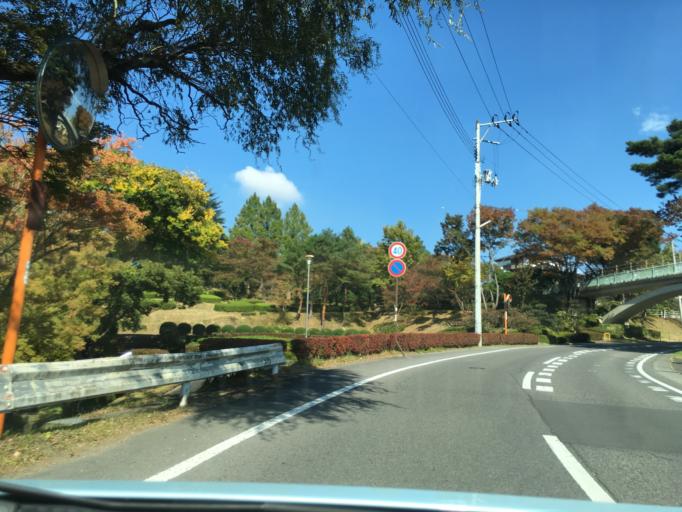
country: JP
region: Fukushima
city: Sukagawa
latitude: 37.2887
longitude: 140.3803
